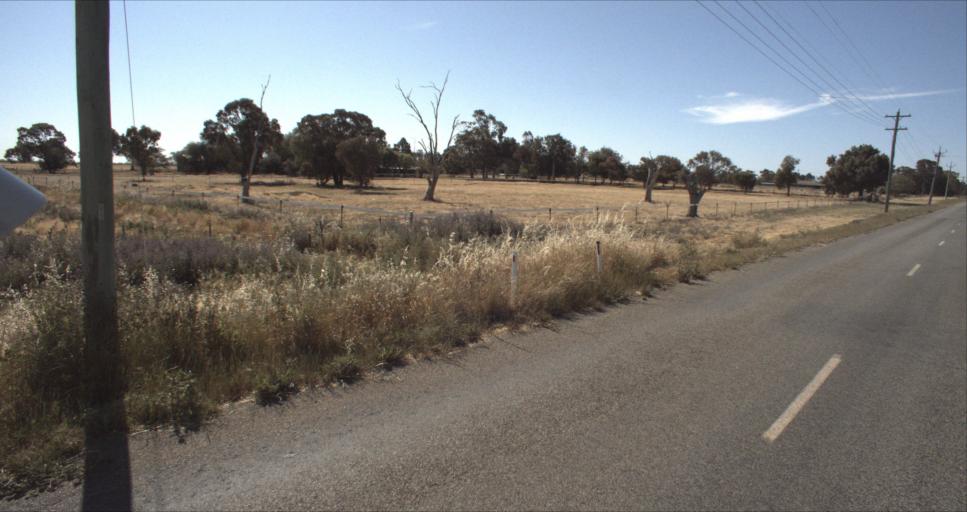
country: AU
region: New South Wales
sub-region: Leeton
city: Leeton
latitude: -34.5680
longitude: 146.3822
